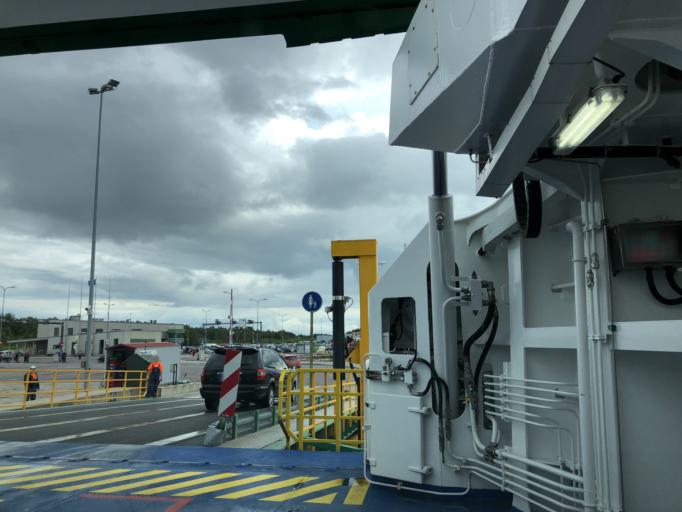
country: EE
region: Laeaene
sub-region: Haapsalu linn
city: Haapsalu
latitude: 58.9066
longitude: 23.4224
